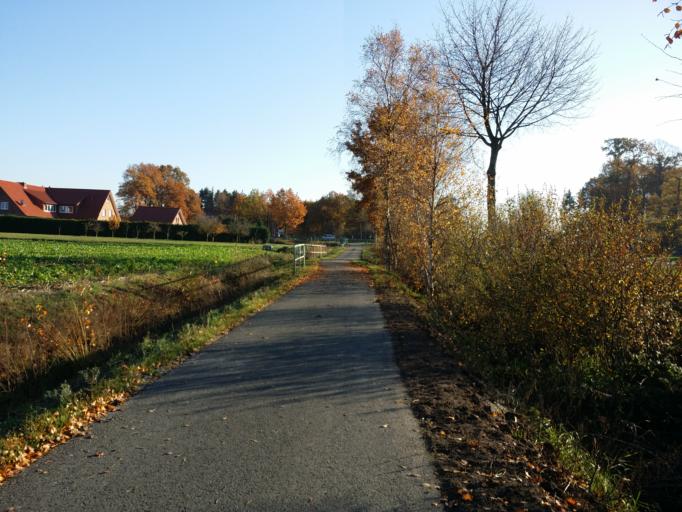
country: DE
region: Lower Saxony
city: Ottersberg
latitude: 53.0498
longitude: 9.1408
